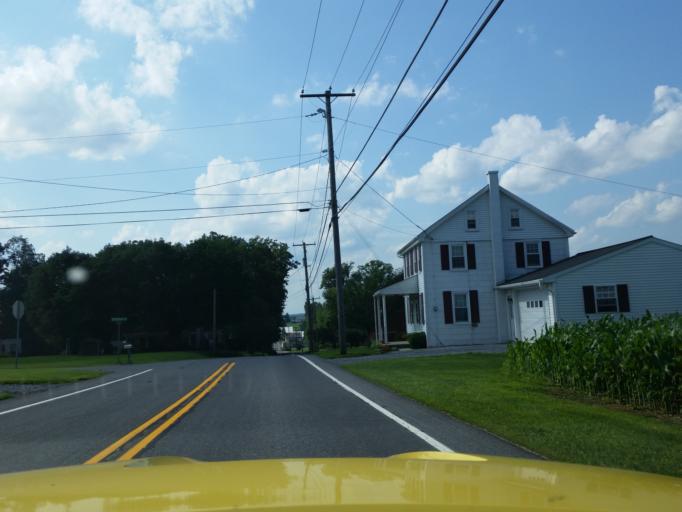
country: US
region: Pennsylvania
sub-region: Lancaster County
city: Manheim
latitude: 40.1715
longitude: -76.4542
